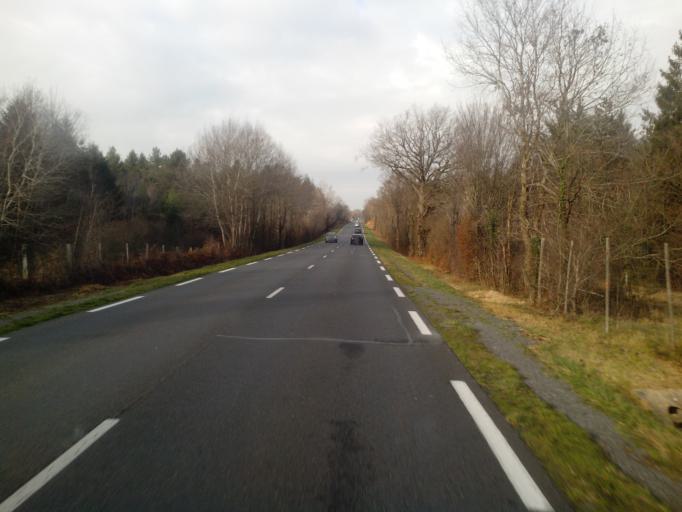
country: FR
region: Limousin
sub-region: Departement de la Haute-Vienne
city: Bussiere-Poitevine
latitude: 46.2566
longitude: 0.8765
